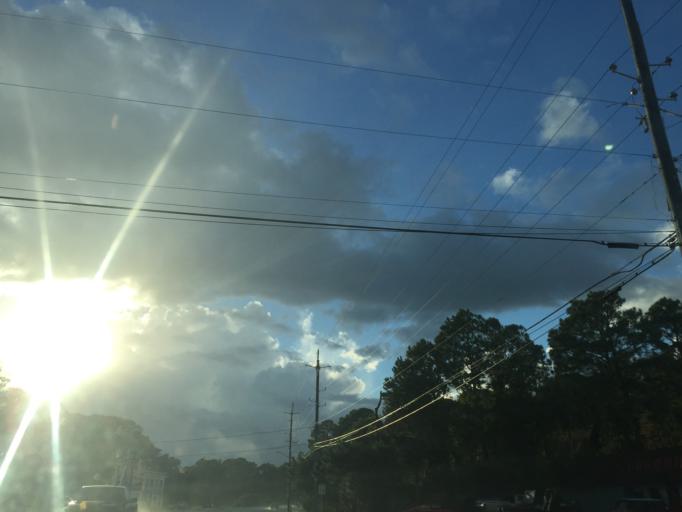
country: US
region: Georgia
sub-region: Chatham County
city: Tybee Island
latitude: 32.0136
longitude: -80.8447
